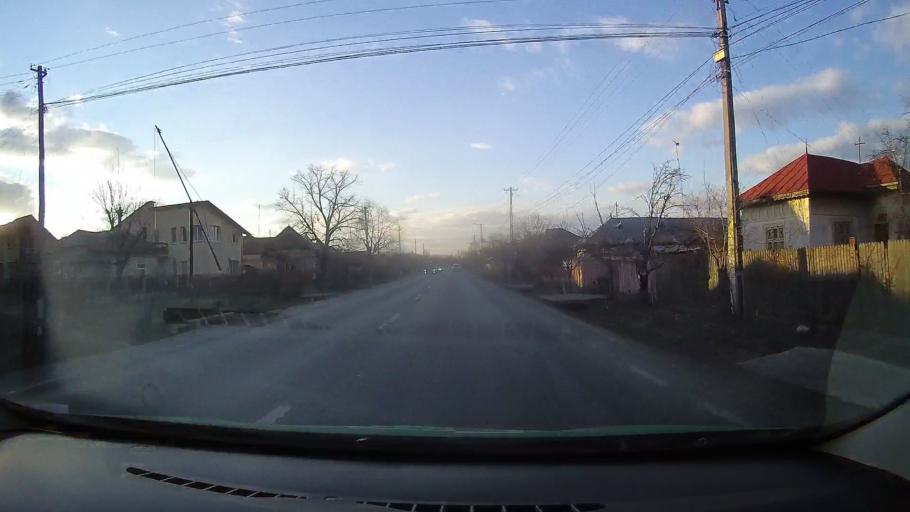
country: RO
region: Dambovita
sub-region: Comuna Gura Ocnitei
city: Adanca
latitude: 44.9088
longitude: 25.6194
